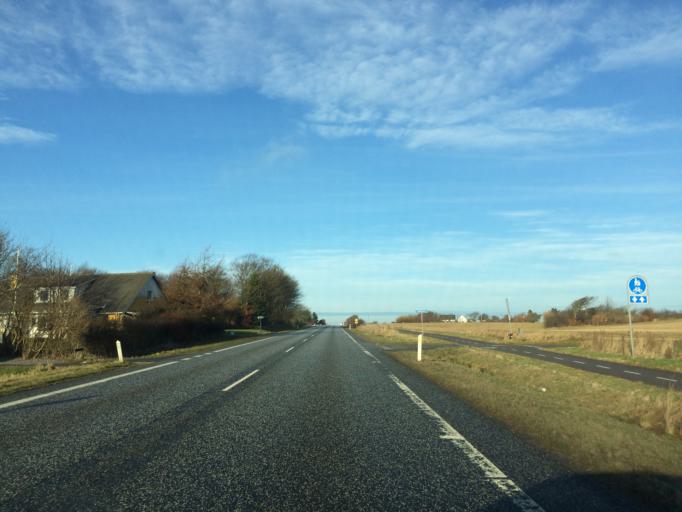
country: DK
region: Central Jutland
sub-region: Struer Kommune
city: Struer
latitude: 56.5268
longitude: 8.5681
